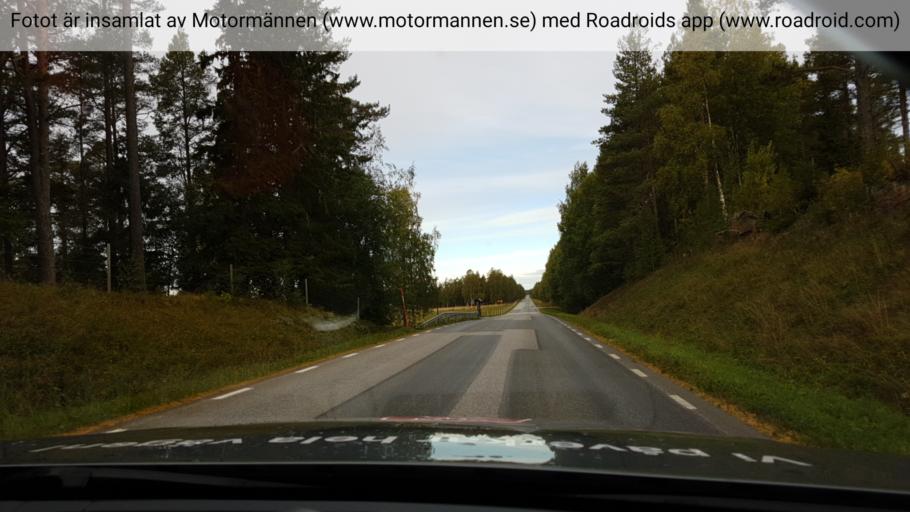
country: SE
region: Jaemtland
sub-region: Krokoms Kommun
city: Krokom
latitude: 63.2894
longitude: 14.2539
